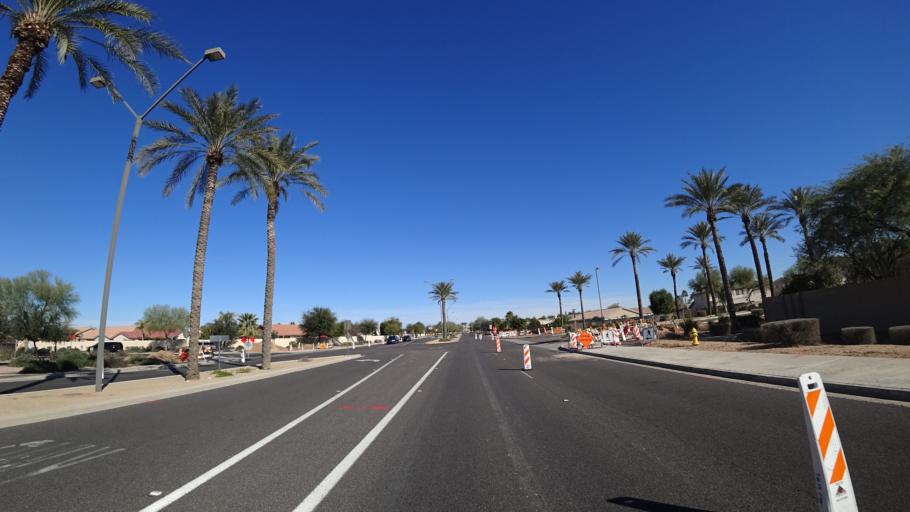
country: US
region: Arizona
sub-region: Maricopa County
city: Litchfield Park
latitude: 33.4824
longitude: -112.3747
